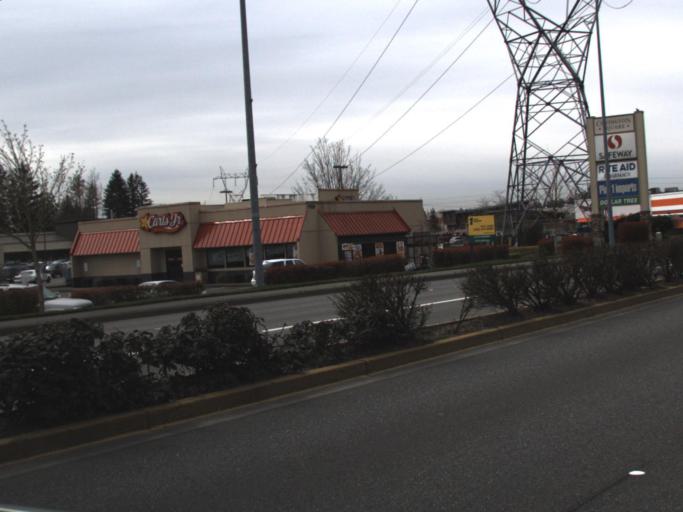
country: US
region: Washington
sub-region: King County
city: Covington
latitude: 47.3582
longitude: -122.1140
